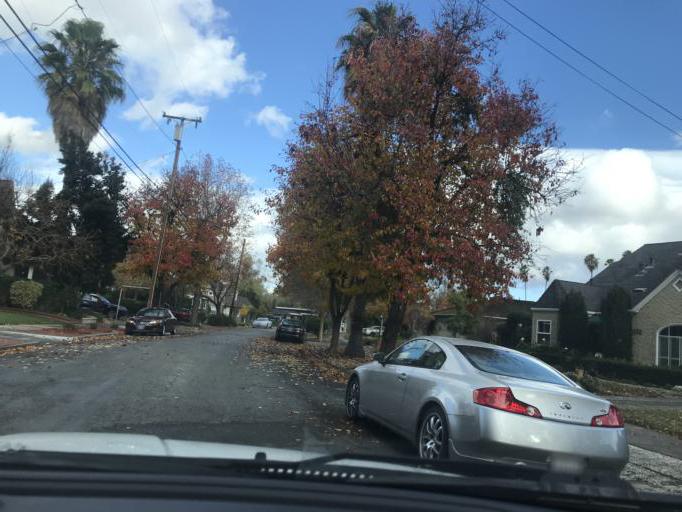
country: US
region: California
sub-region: Santa Clara County
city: Buena Vista
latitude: 37.3154
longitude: -121.9023
